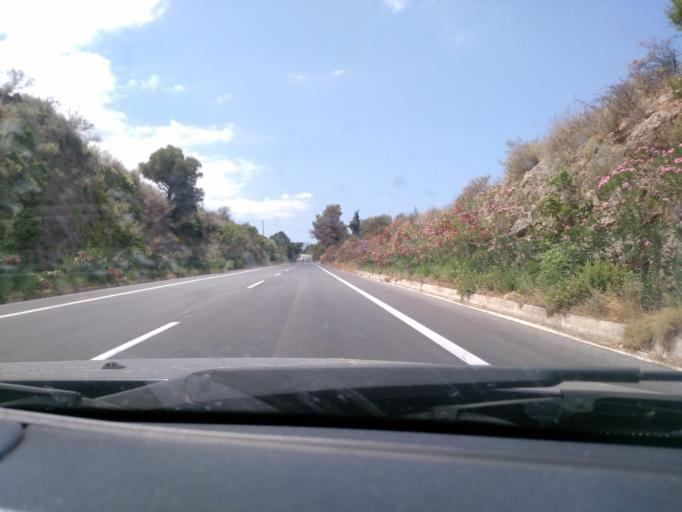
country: GR
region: Crete
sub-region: Nomos Chanias
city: Georgioupolis
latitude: 35.3638
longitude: 24.2393
